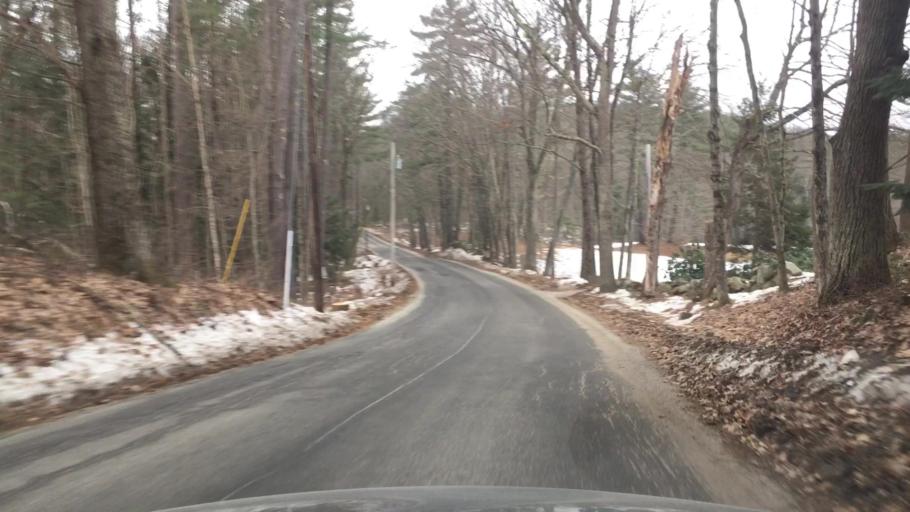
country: US
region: New Hampshire
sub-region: Hillsborough County
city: New Boston
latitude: 43.0069
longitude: -71.6688
